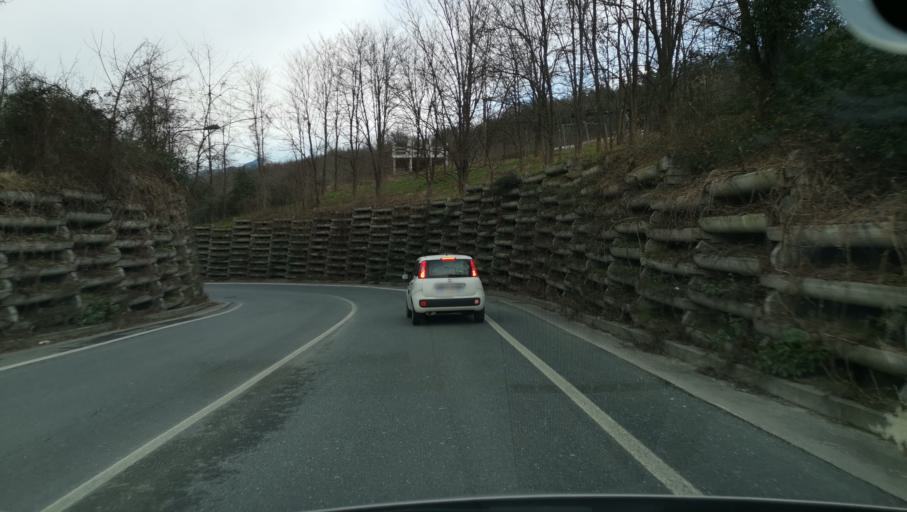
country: IT
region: Piedmont
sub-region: Provincia di Torino
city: Avigliana
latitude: 45.0612
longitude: 7.3925
